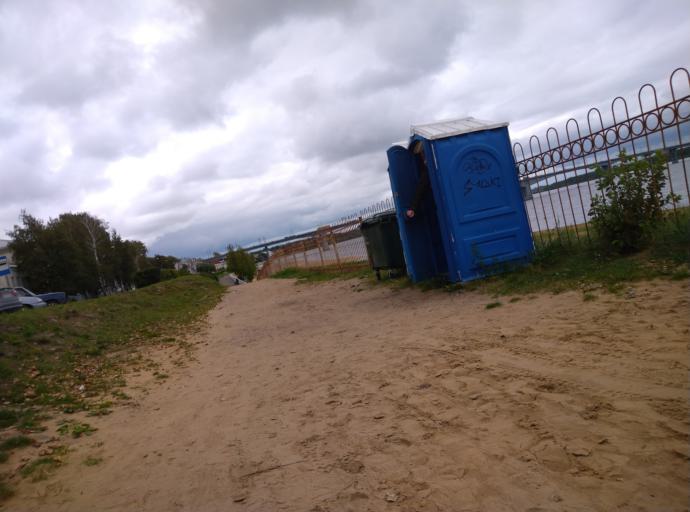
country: RU
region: Kostroma
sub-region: Kostromskoy Rayon
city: Kostroma
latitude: 57.7592
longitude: 40.9352
